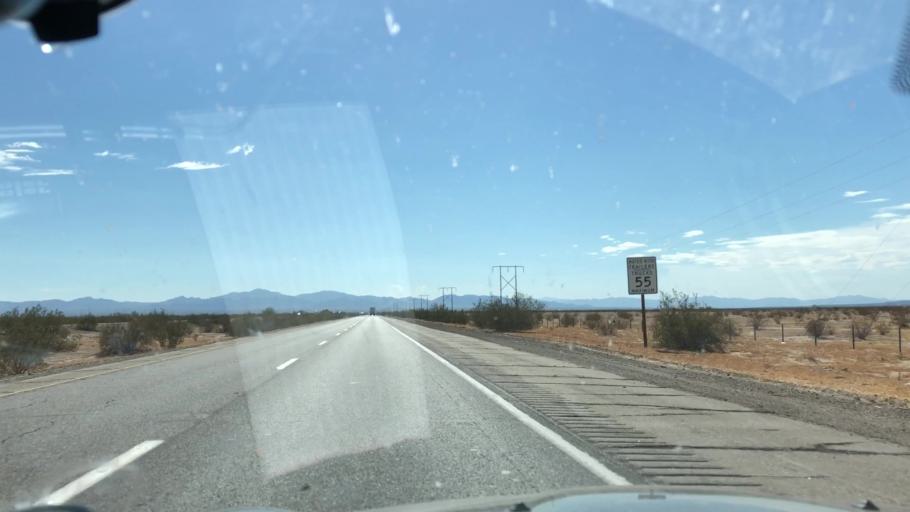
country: US
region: California
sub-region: Riverside County
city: Mesa Verde
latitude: 33.6062
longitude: -114.9284
